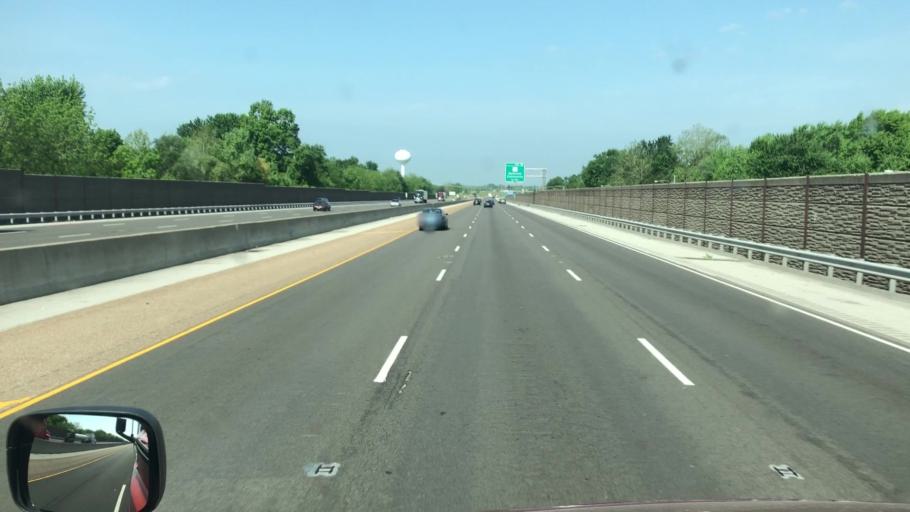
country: US
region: Illinois
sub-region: Saint Clair County
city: Fairview Heights
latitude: 38.5993
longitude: -89.9684
